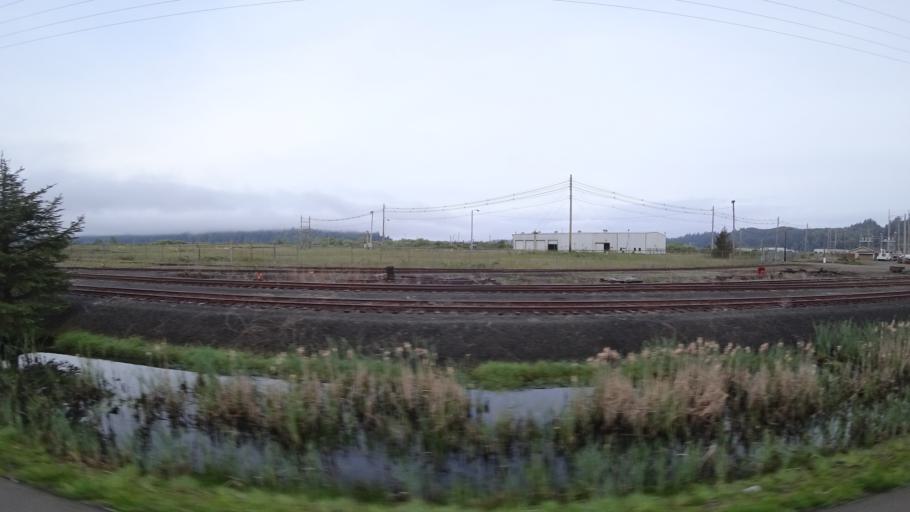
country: US
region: Oregon
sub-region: Douglas County
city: Reedsport
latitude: 43.7397
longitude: -124.1111
